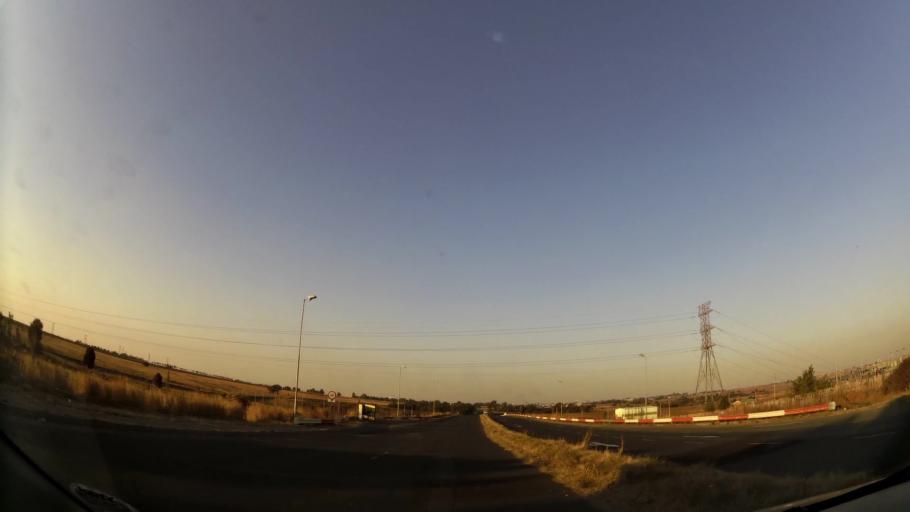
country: ZA
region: Gauteng
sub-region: West Rand District Municipality
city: Randfontein
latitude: -26.2057
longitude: 27.6617
